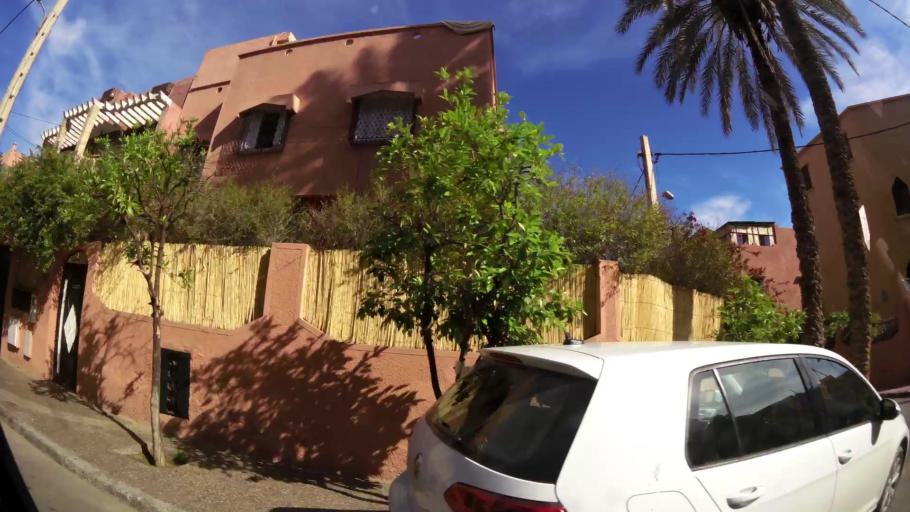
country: MA
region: Marrakech-Tensift-Al Haouz
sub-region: Marrakech
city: Marrakesh
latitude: 31.6443
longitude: -8.0077
